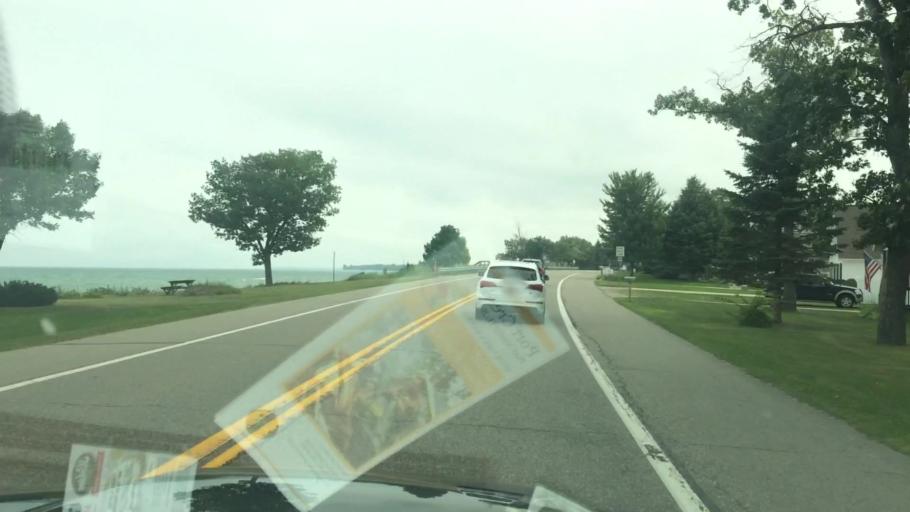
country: US
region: Michigan
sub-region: Huron County
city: Pigeon
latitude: 43.9858
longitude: -83.1650
